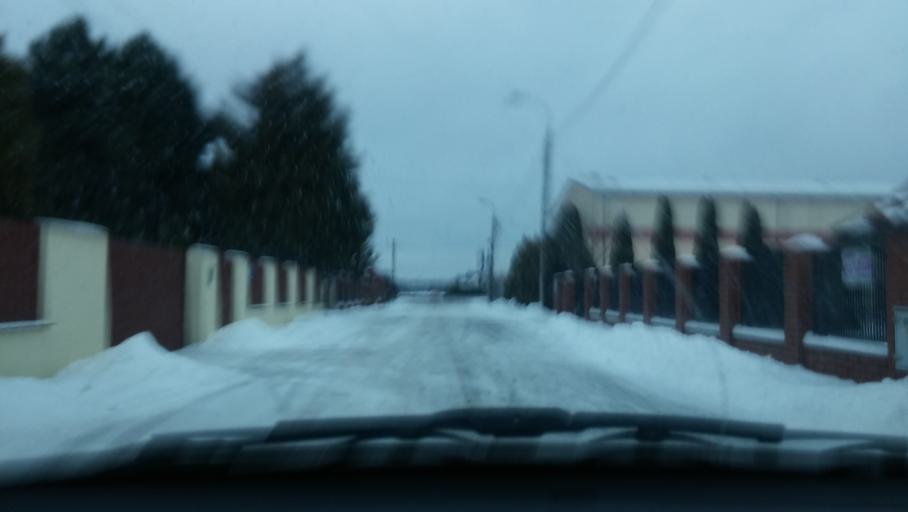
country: PL
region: Masovian Voivodeship
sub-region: Powiat warszawski zachodni
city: Babice
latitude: 52.2419
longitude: 20.8702
